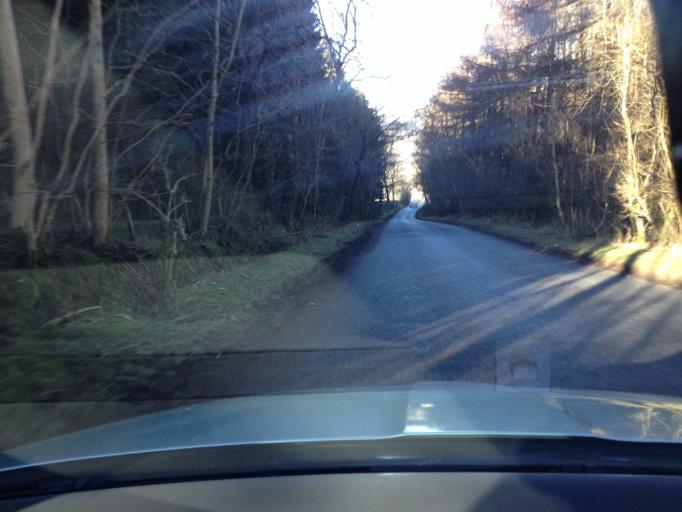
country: GB
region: Scotland
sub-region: Perth and Kinross
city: Bridge of Earn
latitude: 56.3175
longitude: -3.3696
